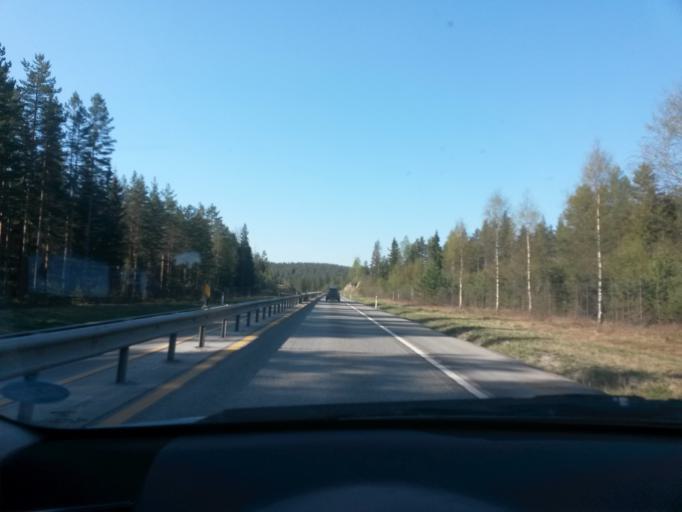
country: NO
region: Buskerud
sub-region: Kongsberg
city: Kongsberg
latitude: 59.6801
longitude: 9.7401
